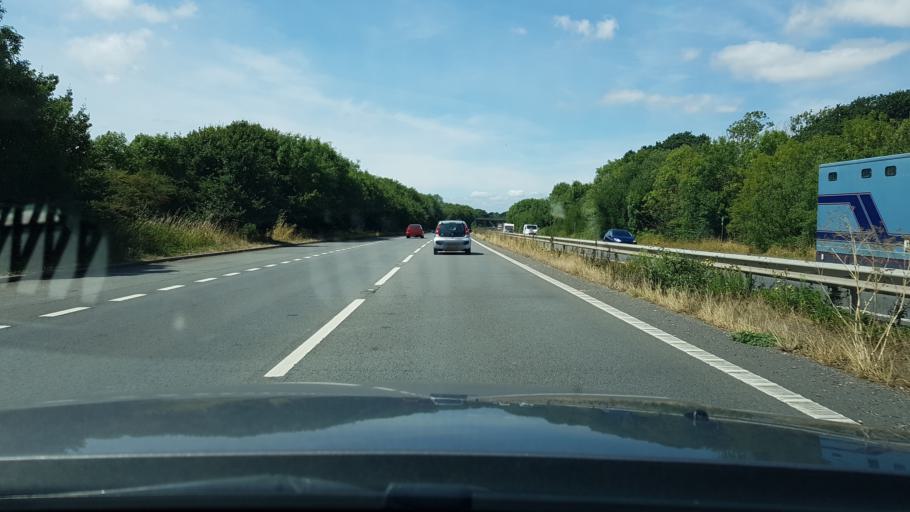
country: GB
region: England
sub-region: West Sussex
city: Bosham
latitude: 50.8511
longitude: -0.8608
